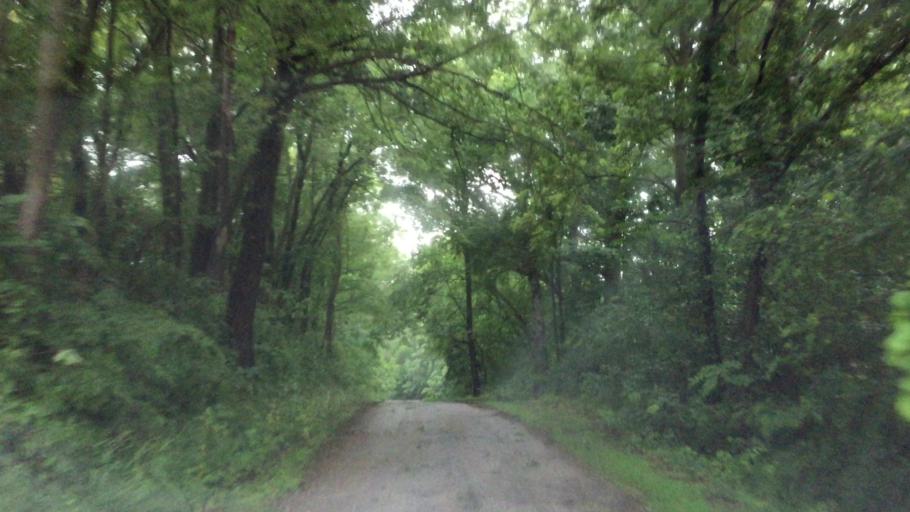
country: US
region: Iowa
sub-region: Lee County
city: Fort Madison
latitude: 40.6065
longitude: -91.2754
